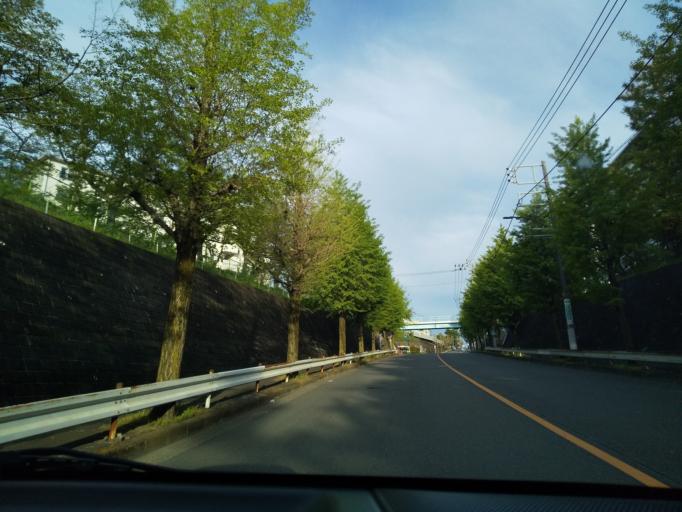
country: JP
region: Tokyo
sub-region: Machida-shi
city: Machida
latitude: 35.5713
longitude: 139.4505
